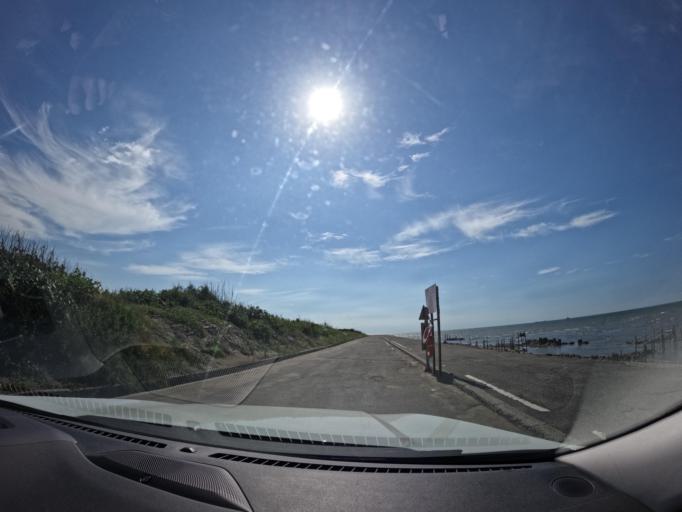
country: TW
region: Taiwan
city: Taoyuan City
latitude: 25.0934
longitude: 121.1881
